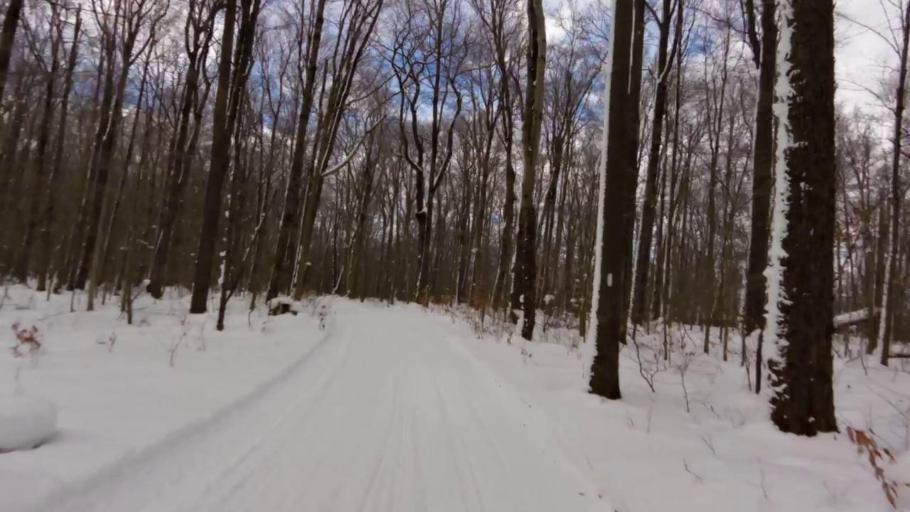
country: US
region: New York
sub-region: Cattaraugus County
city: Salamanca
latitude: 42.0494
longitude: -78.7604
